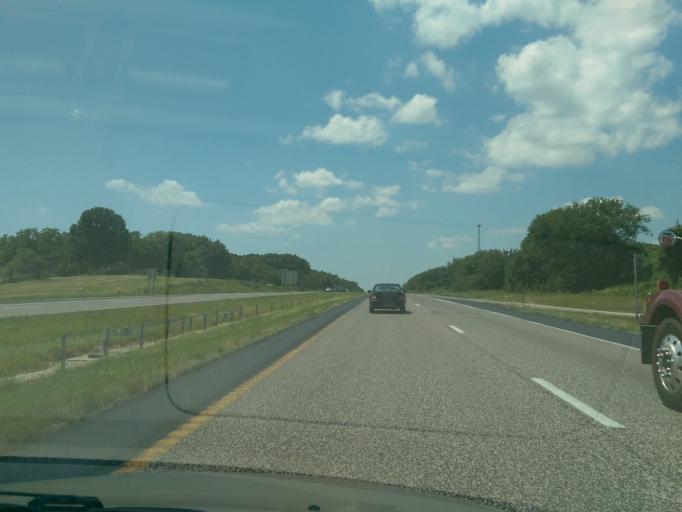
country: US
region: Missouri
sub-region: Cooper County
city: Boonville
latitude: 38.9397
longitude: -92.5990
